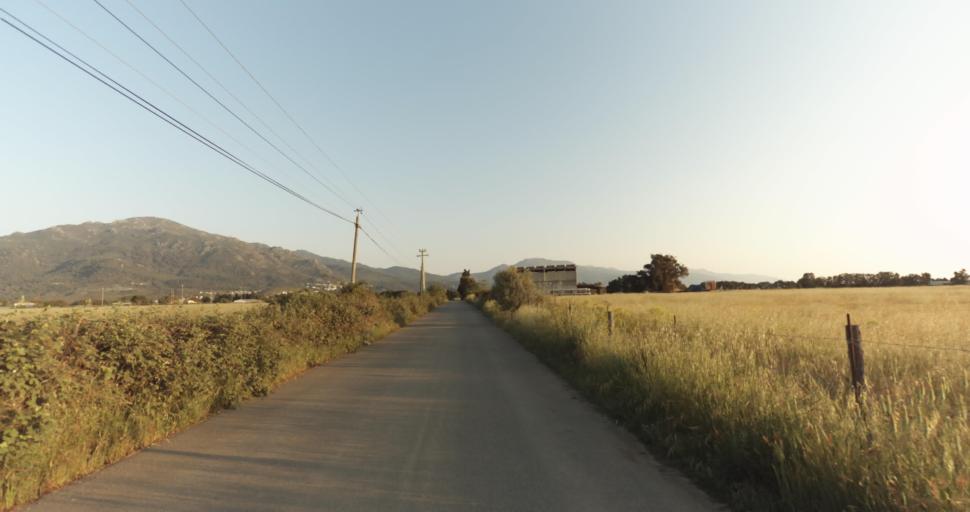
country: FR
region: Corsica
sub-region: Departement de la Haute-Corse
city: Biguglia
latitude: 42.6064
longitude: 9.4511
